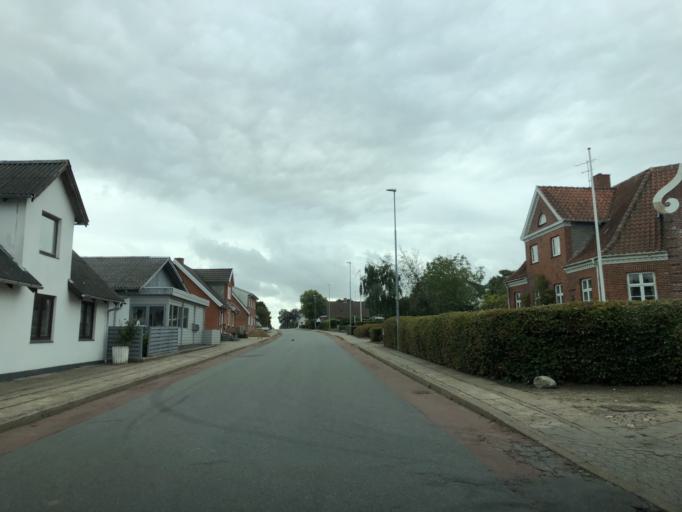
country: DK
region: North Denmark
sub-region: Thisted Kommune
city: Thisted
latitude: 56.8896
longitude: 8.5931
